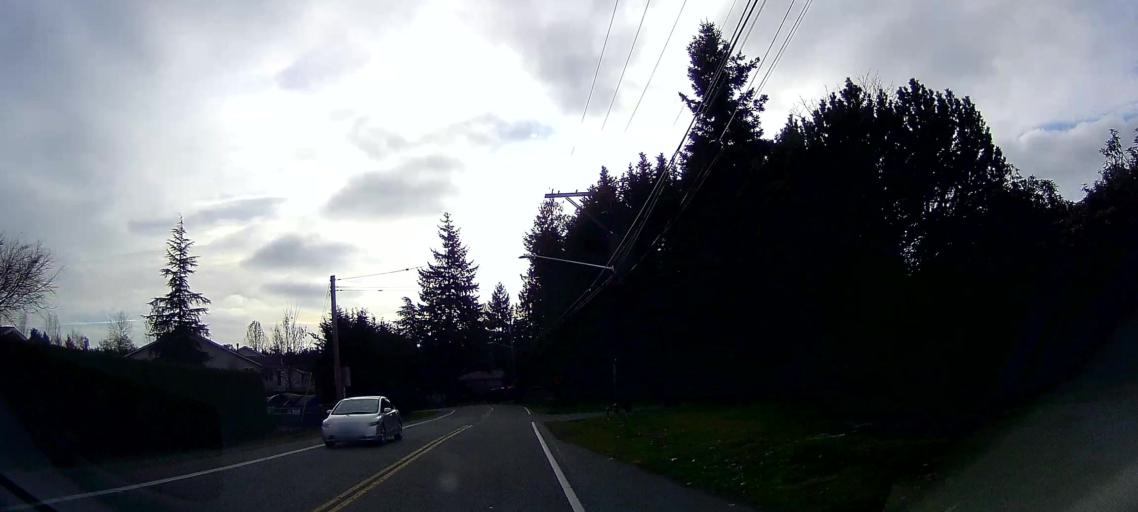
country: US
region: Washington
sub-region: Snohomish County
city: Alderwood Manor
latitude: 47.8117
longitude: -122.2713
